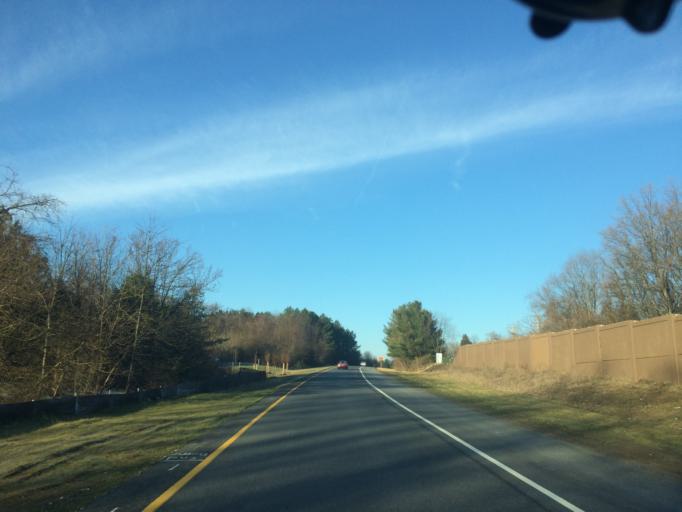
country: US
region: Maryland
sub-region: Howard County
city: Riverside
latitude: 39.1841
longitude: -76.8743
